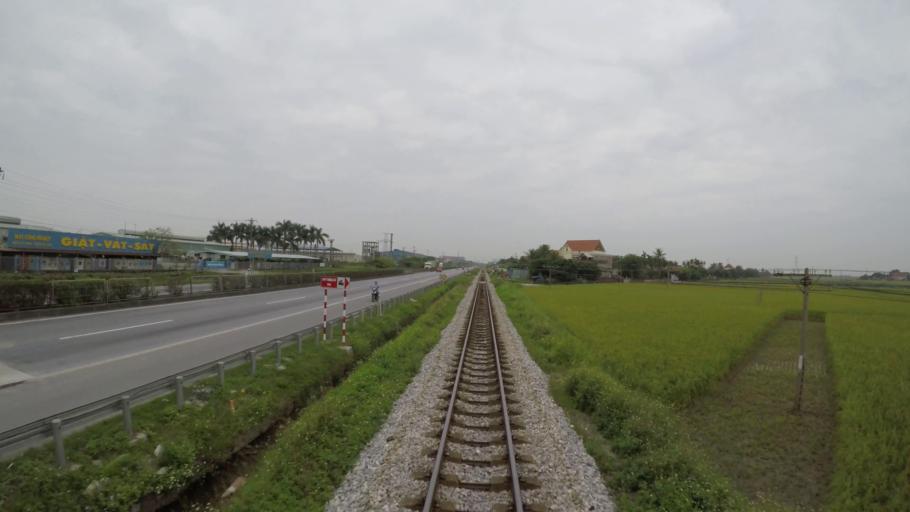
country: VN
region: Hai Duong
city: Phu Thai
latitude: 20.9478
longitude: 106.5365
